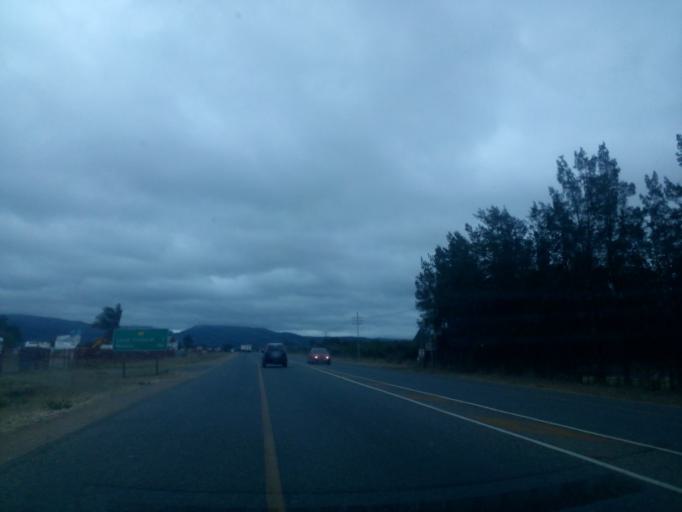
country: ZA
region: Limpopo
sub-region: Vhembe District Municipality
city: Louis Trichardt
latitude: -23.0759
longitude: 29.9094
